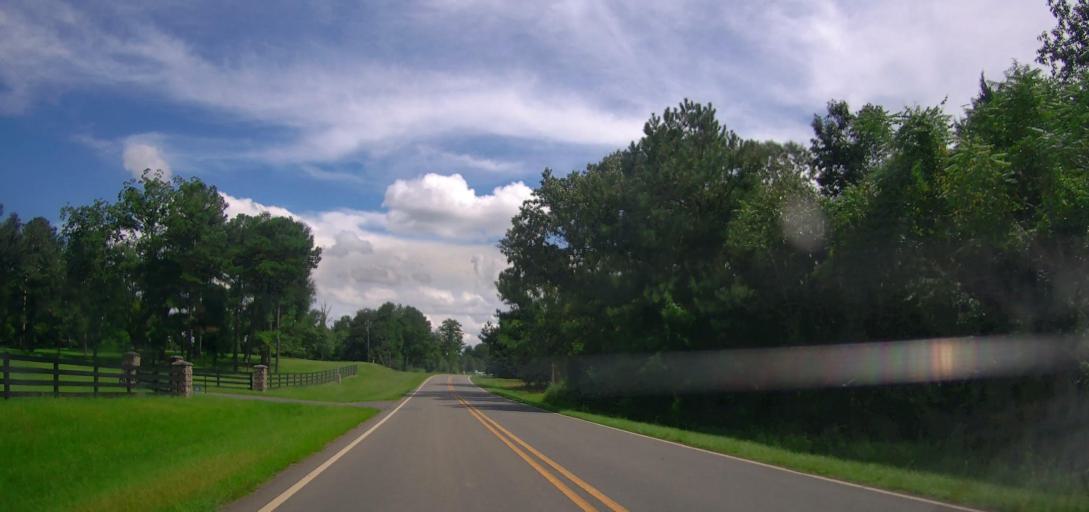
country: US
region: Georgia
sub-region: Taylor County
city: Butler
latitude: 32.5335
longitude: -84.2128
